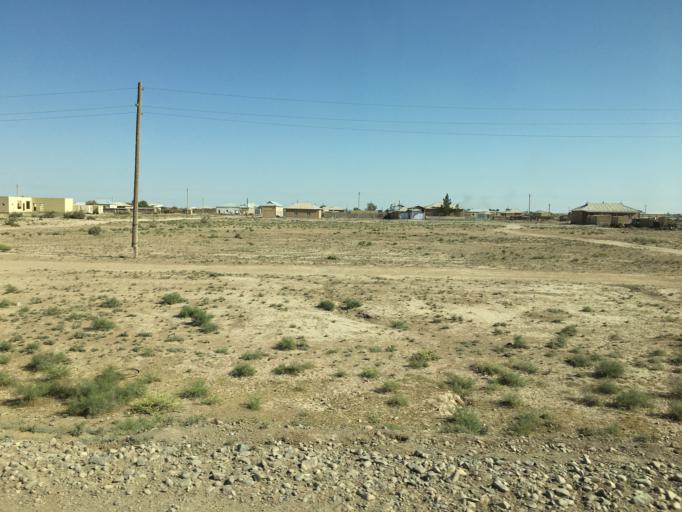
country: IR
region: Razavi Khorasan
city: Sarakhs
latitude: 36.5745
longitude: 61.2637
